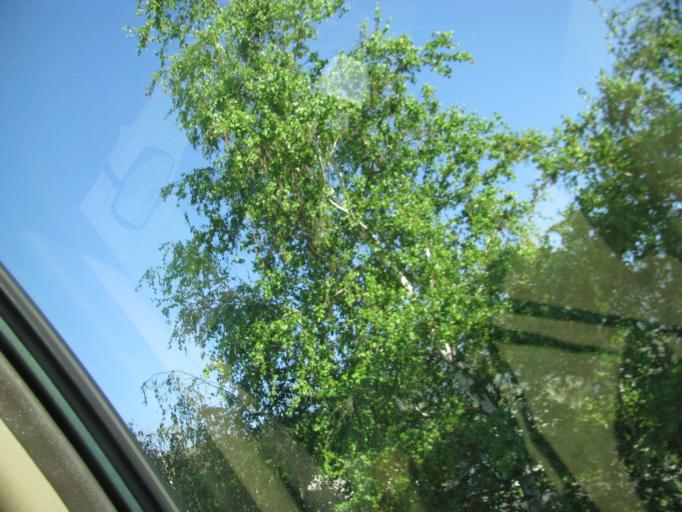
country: US
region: Washington
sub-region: Spokane County
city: Liberty Lake
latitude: 47.6288
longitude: -117.1196
